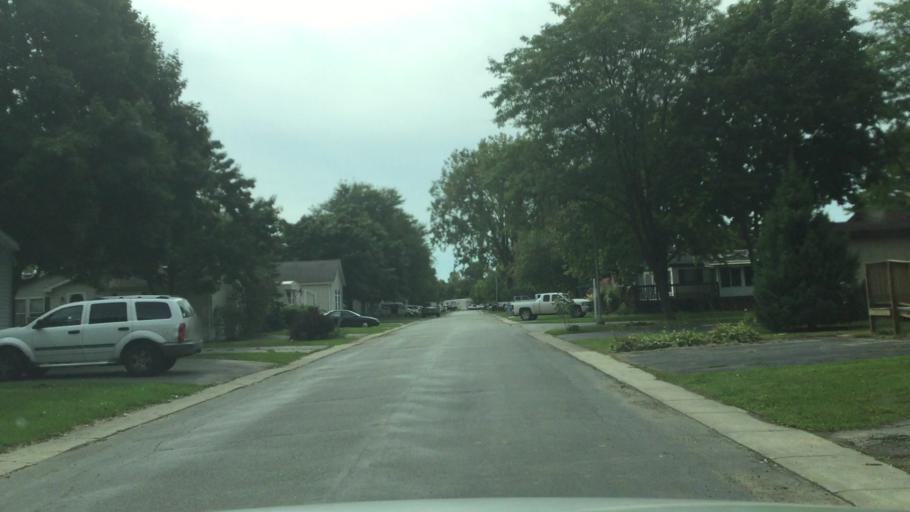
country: US
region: Michigan
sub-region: Oakland County
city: Holly
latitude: 42.8111
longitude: -83.6241
